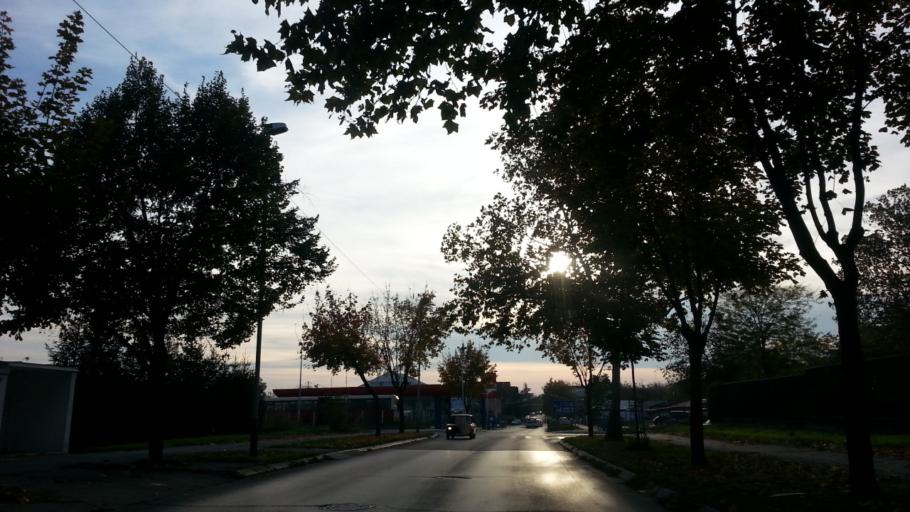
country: RS
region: Central Serbia
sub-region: Belgrade
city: Zemun
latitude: 44.8141
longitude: 20.3813
